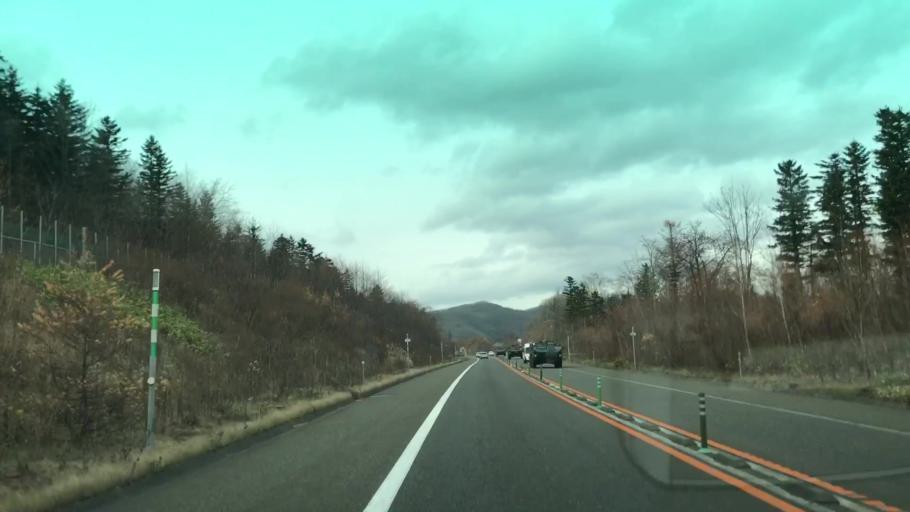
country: JP
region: Hokkaido
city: Otofuke
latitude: 43.0122
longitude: 142.8328
